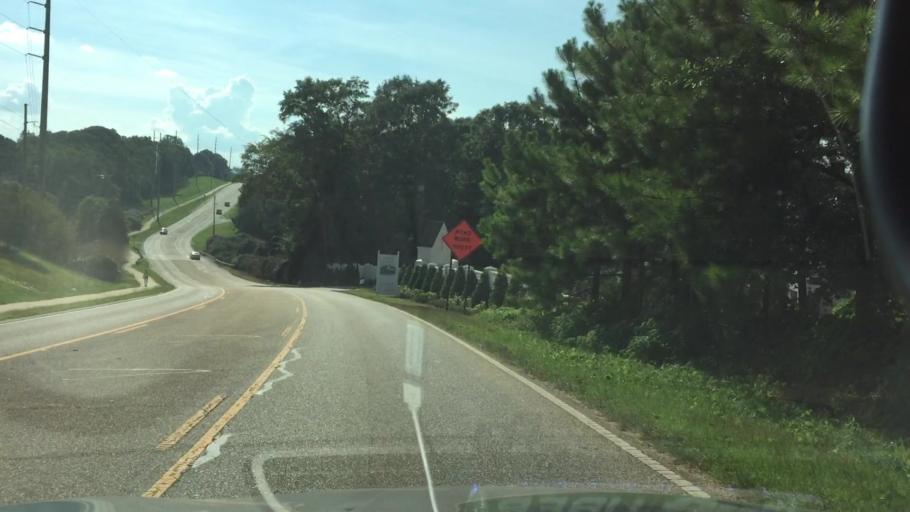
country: US
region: Alabama
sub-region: Lee County
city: Auburn
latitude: 32.5859
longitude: -85.4477
